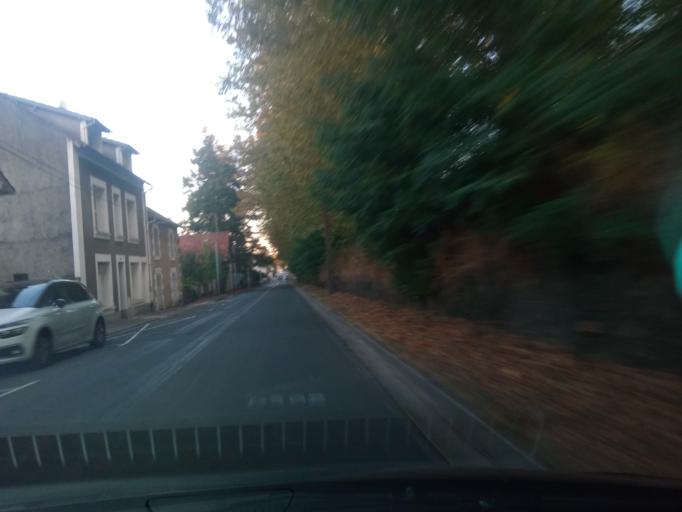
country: FR
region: Poitou-Charentes
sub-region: Departement de la Vienne
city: Montmorillon
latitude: 46.4176
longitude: 0.8743
